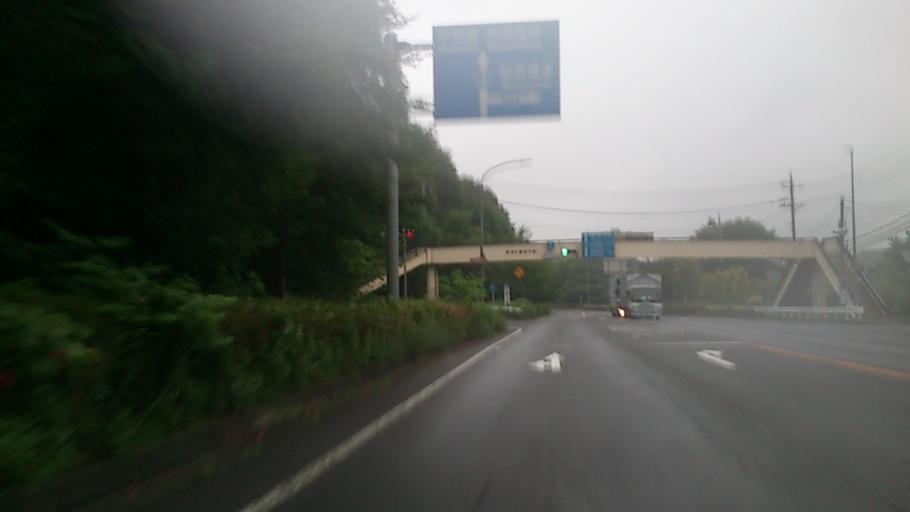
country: JP
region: Tochigi
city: Kuroiso
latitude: 37.0591
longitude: 140.1083
